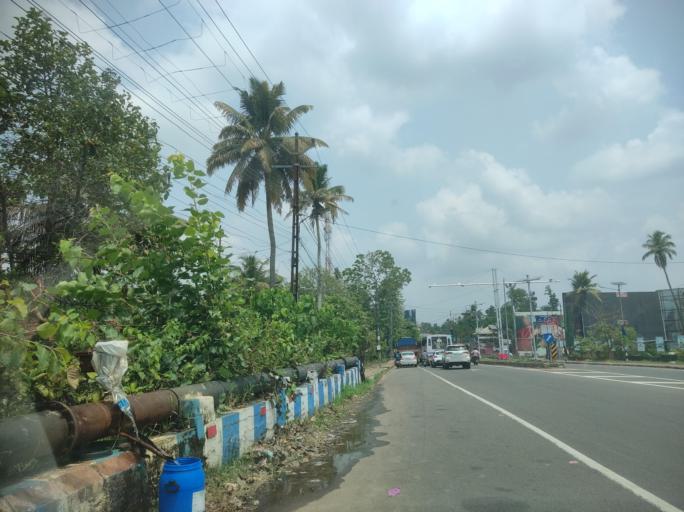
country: IN
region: Kerala
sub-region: Kottayam
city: Changanacheri
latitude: 9.4293
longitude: 76.5447
